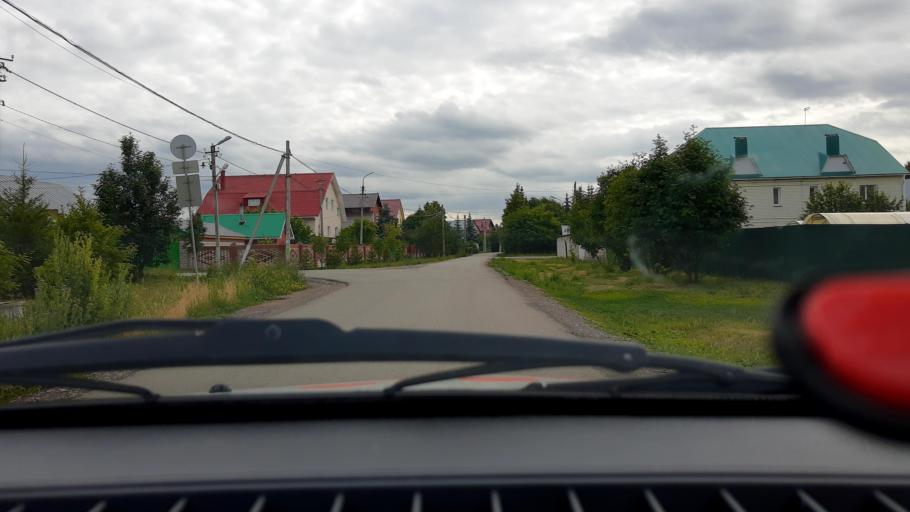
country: RU
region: Bashkortostan
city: Avdon
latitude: 54.4931
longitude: 55.8973
